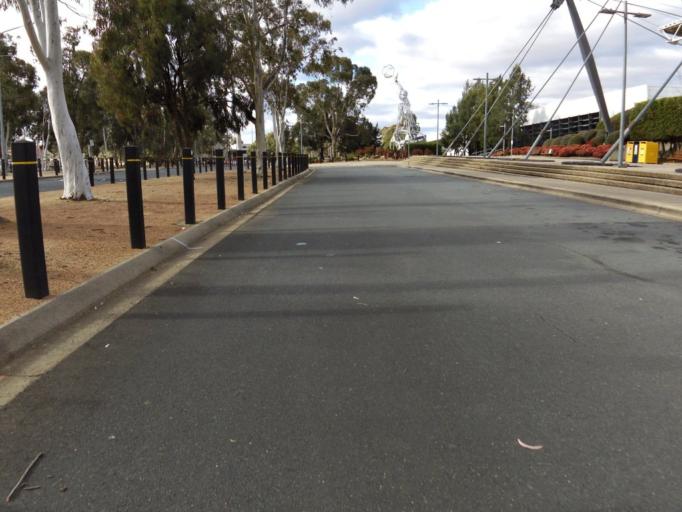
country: AU
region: Australian Capital Territory
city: Kaleen
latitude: -35.2475
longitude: 149.1004
